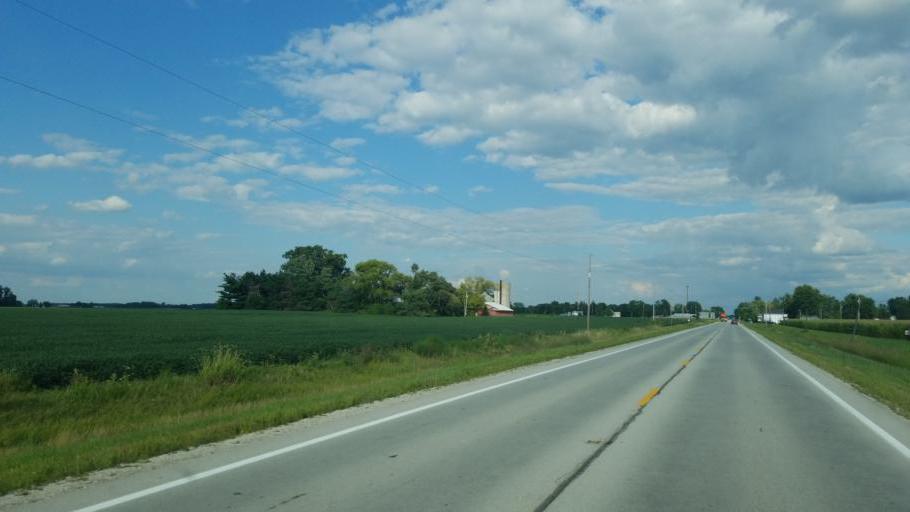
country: US
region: Ohio
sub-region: Sandusky County
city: Gibsonburg
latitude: 41.3413
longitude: -83.3864
